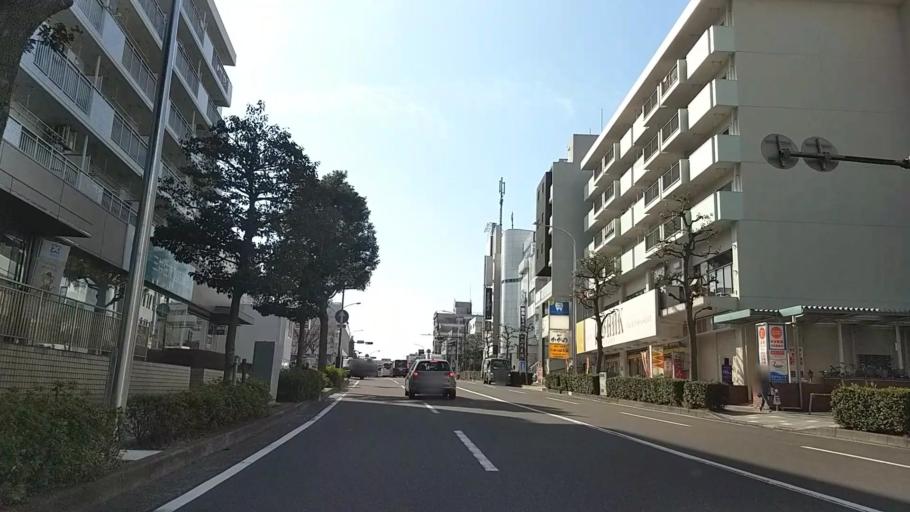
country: JP
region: Kanagawa
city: Kamakura
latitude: 35.3764
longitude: 139.5758
